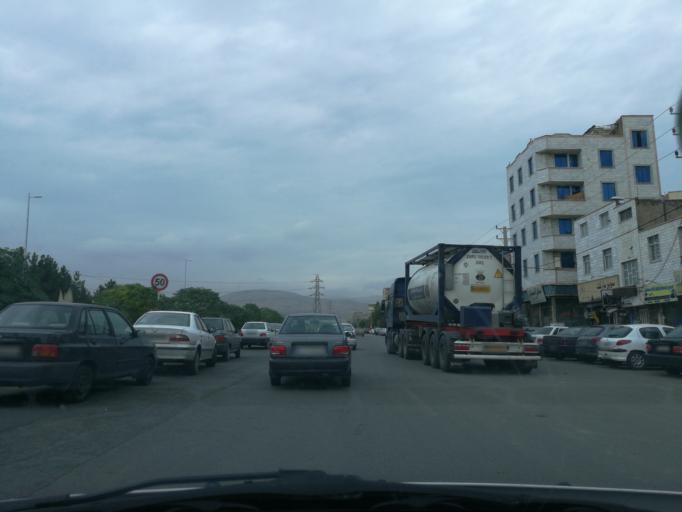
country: IR
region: Alborz
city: Karaj
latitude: 35.8480
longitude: 50.9160
